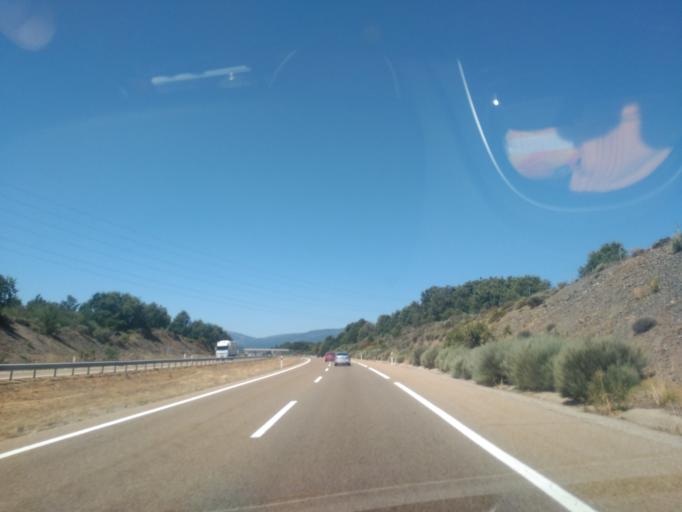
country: ES
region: Castille and Leon
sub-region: Provincia de Zamora
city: Robleda-Cervantes
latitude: 42.0560
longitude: -6.5670
